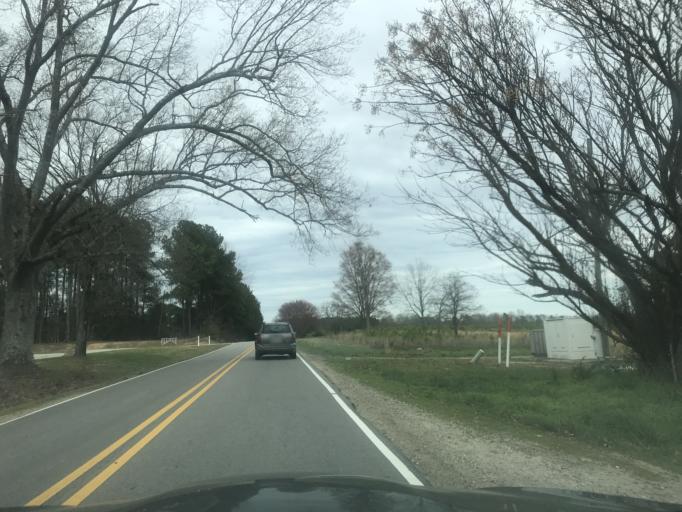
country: US
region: North Carolina
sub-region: Franklin County
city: Franklinton
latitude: 36.1145
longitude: -78.4867
